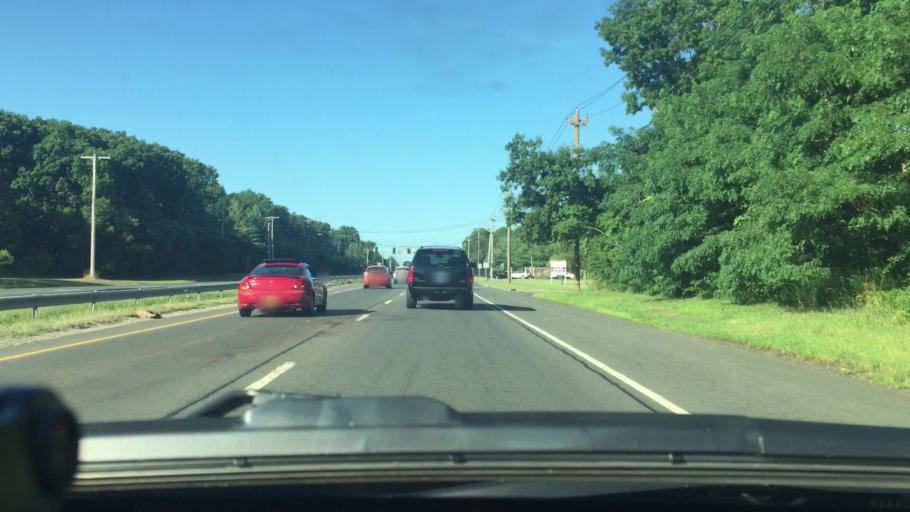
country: US
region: New York
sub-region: Suffolk County
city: Terryville
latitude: 40.8982
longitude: -73.0821
